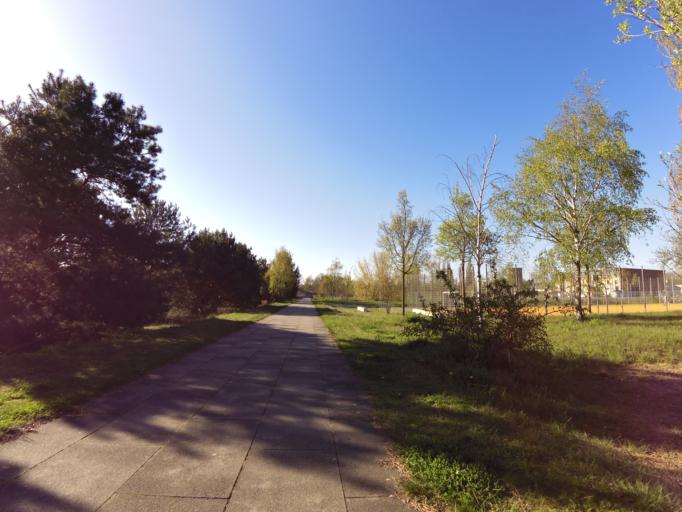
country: DE
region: Berlin
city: Johannisthal
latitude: 52.4403
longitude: 13.5166
